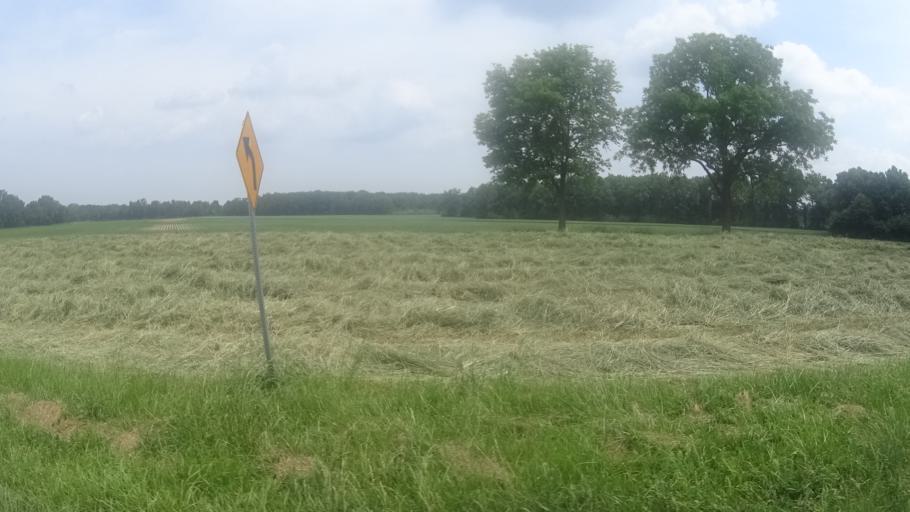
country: US
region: Ohio
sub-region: Erie County
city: Milan
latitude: 41.3447
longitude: -82.6755
